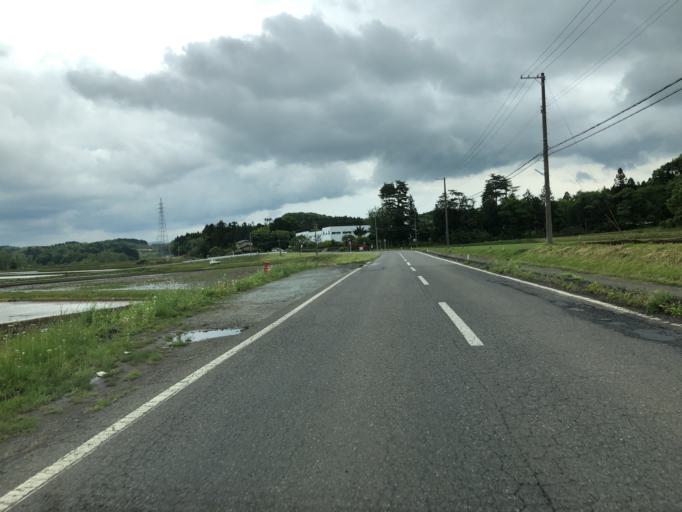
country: JP
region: Fukushima
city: Ishikawa
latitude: 37.1865
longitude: 140.3970
